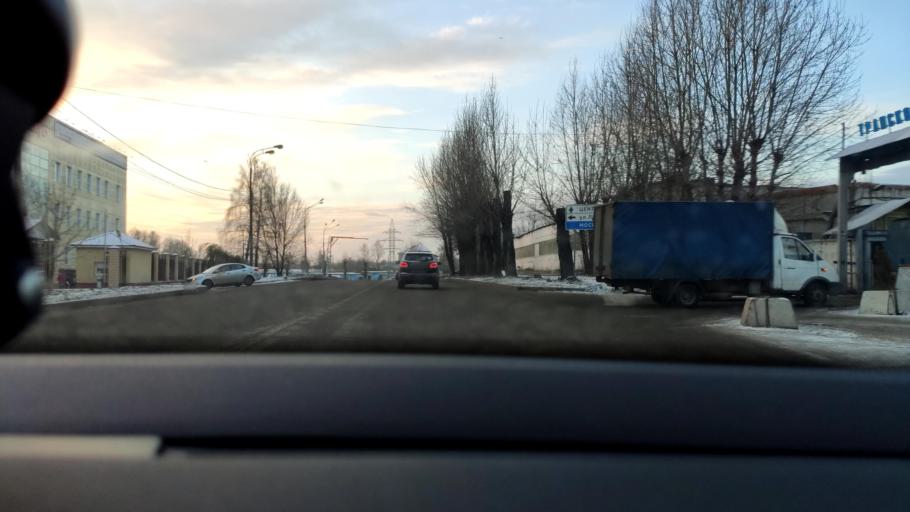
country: RU
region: Moskovskaya
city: Kotel'niki
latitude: 55.6412
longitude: 37.8393
